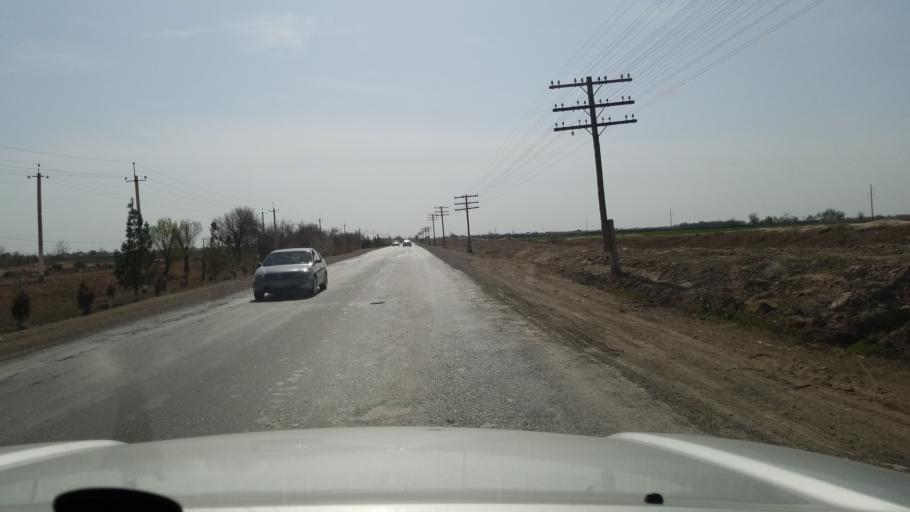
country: TM
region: Lebap
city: Sayat
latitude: 38.8059
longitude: 63.8459
